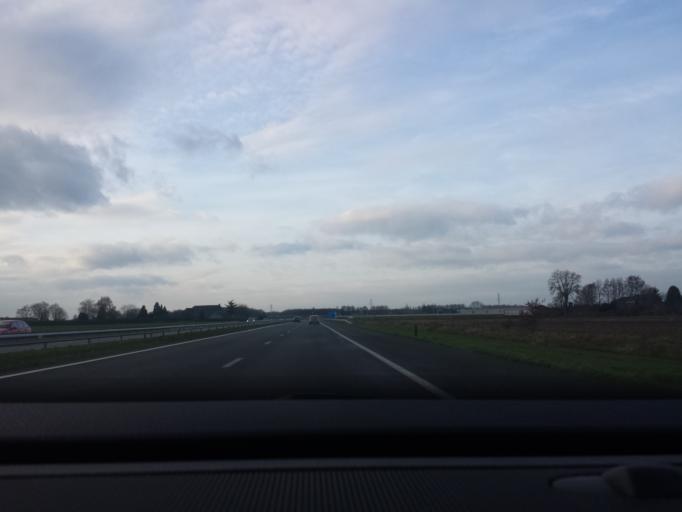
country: NL
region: Gelderland
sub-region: Gemeente Doetinchem
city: Doetinchem
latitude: 51.9445
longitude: 6.2364
